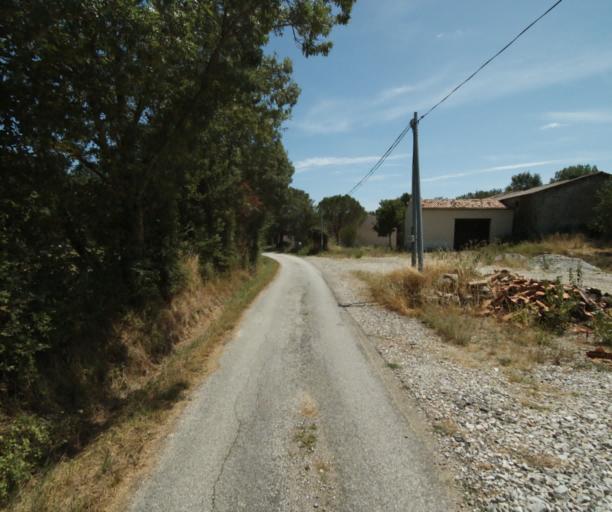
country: FR
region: Midi-Pyrenees
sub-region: Departement de la Haute-Garonne
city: Revel
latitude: 43.4994
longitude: 2.0290
